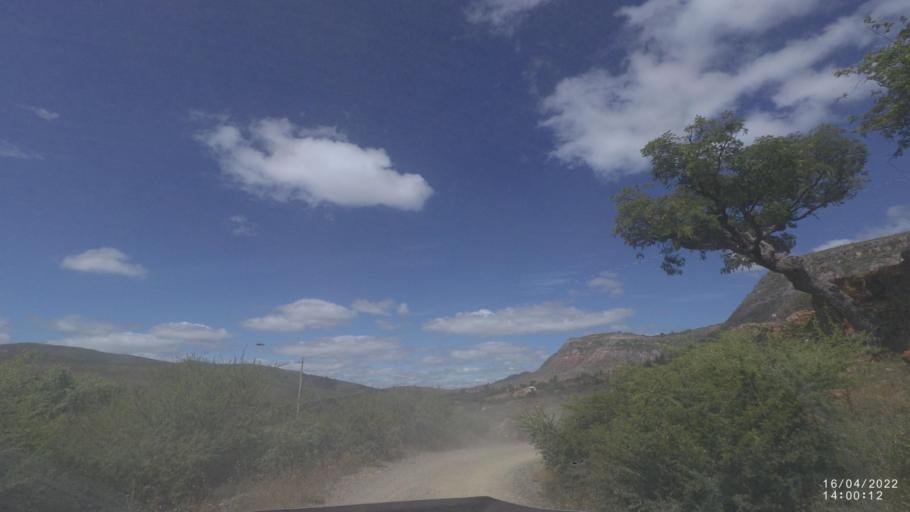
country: BO
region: Cochabamba
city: Mizque
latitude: -18.0421
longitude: -65.5559
